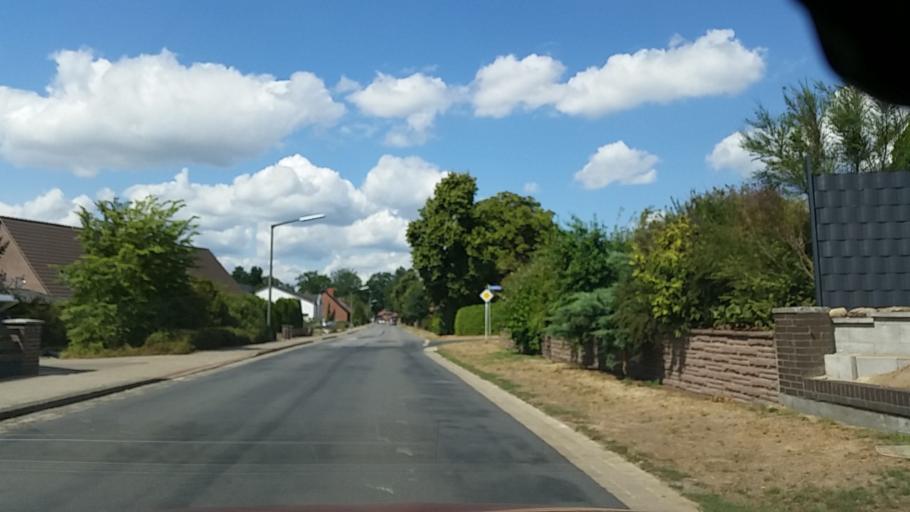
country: DE
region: Lower Saxony
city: Hankensbuttel
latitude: 52.7170
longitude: 10.6223
